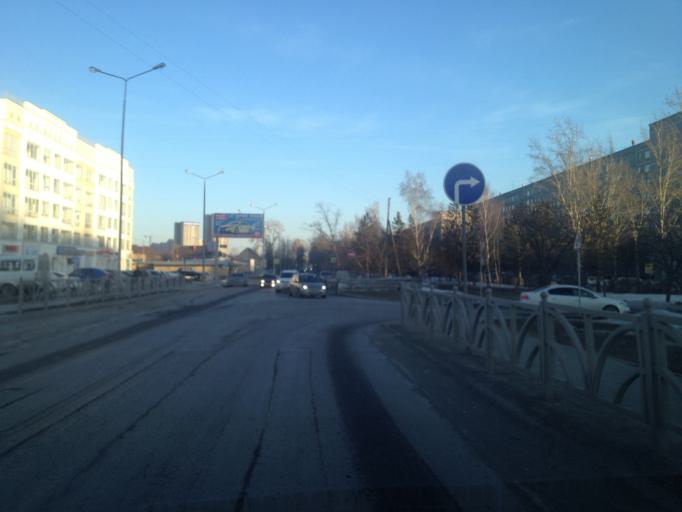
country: RU
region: Sverdlovsk
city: Sovkhoznyy
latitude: 56.8054
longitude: 60.5761
